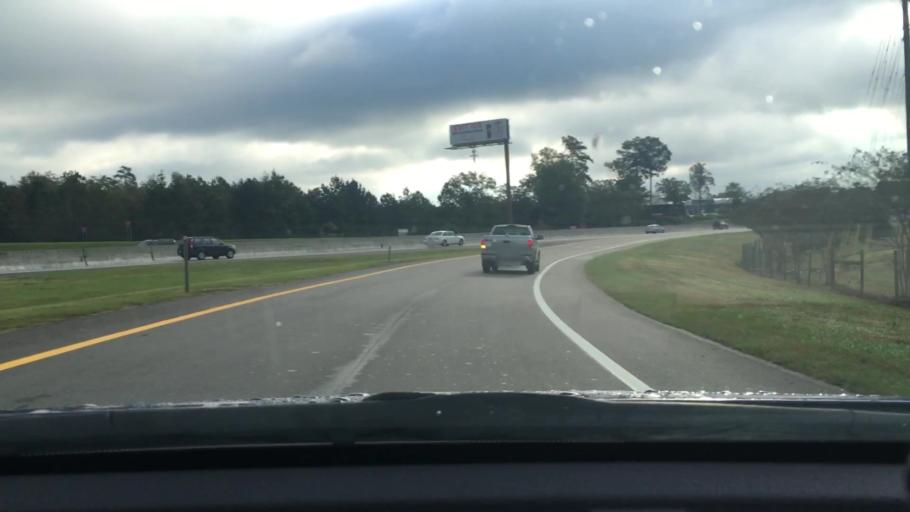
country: US
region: South Carolina
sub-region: Lexington County
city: Irmo
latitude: 34.0974
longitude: -81.1739
